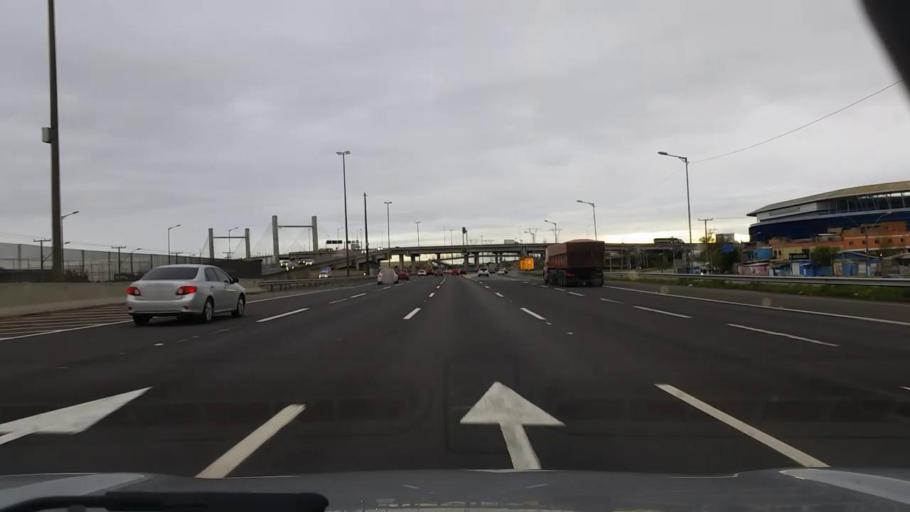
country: BR
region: Rio Grande do Sul
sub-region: Porto Alegre
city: Porto Alegre
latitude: -29.9781
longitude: -51.2001
